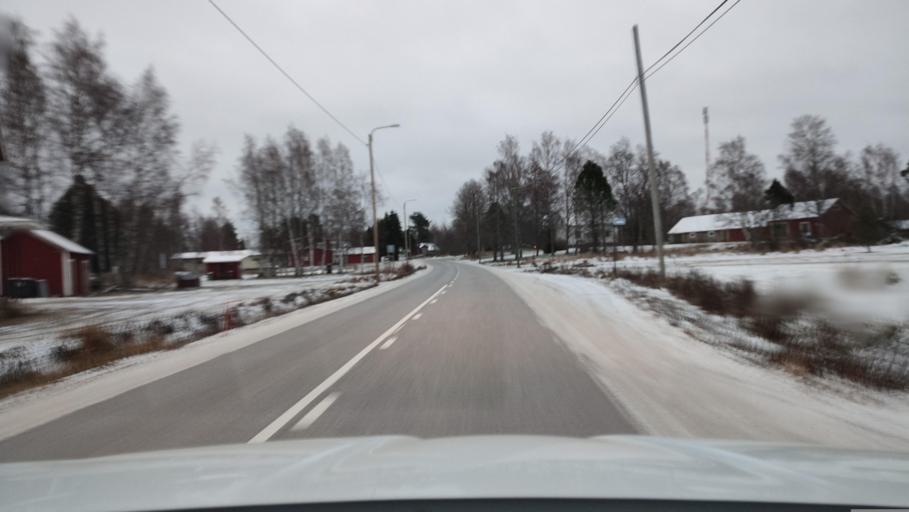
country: FI
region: Ostrobothnia
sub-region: Vaasa
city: Replot
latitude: 63.3453
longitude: 21.3194
